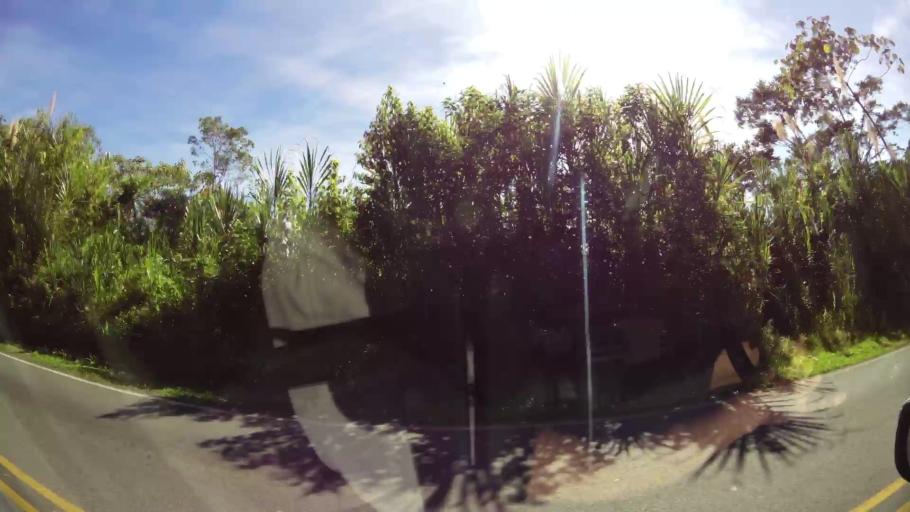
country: CR
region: San Jose
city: San Isidro
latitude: 9.4398
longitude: -83.7122
